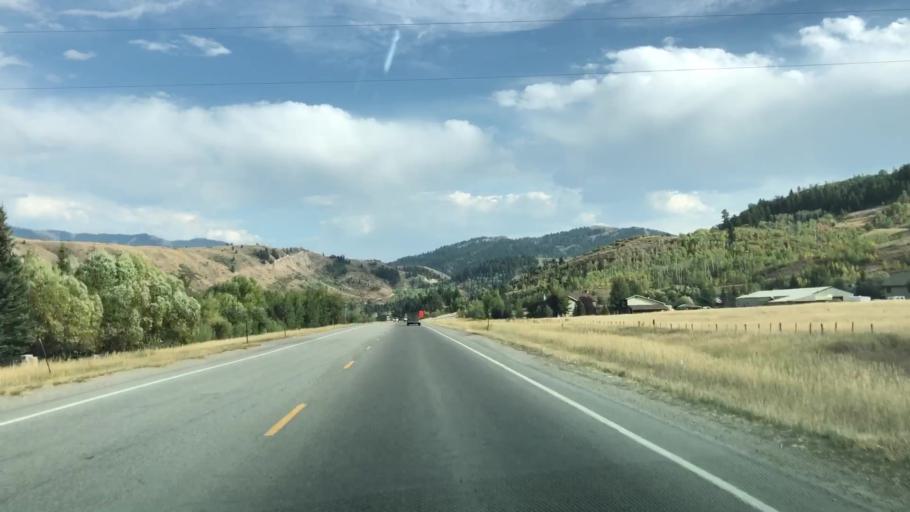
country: US
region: Wyoming
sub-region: Teton County
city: South Park
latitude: 43.3658
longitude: -110.7325
